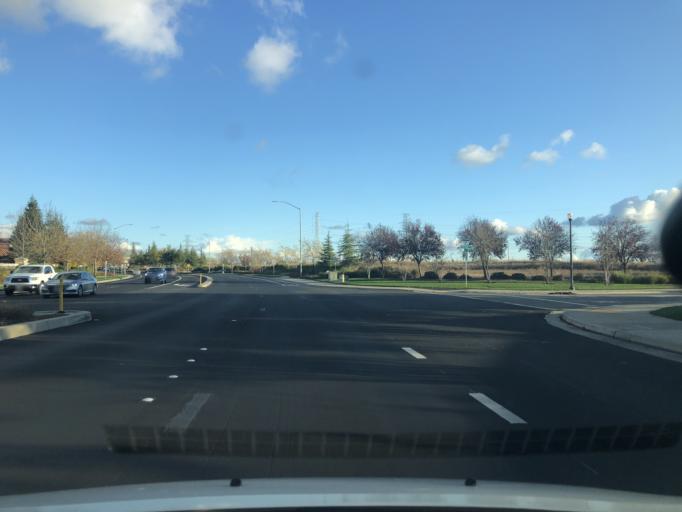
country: US
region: California
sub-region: Sacramento County
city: Antelope
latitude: 38.7671
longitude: -121.3628
